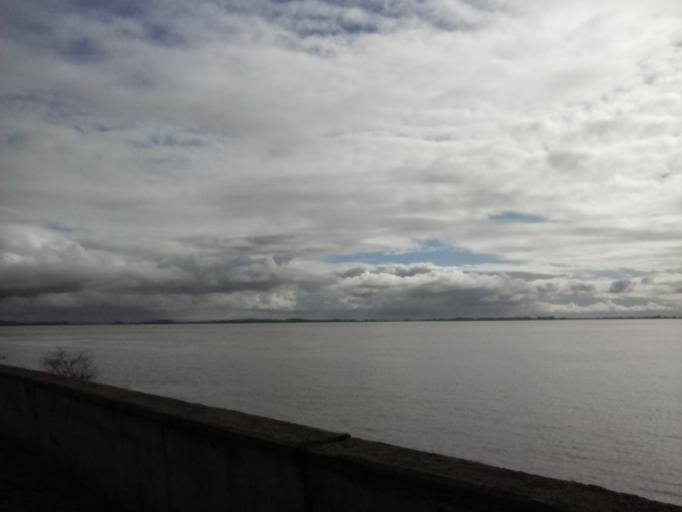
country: BR
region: Rio Grande do Sul
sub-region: Porto Alegre
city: Porto Alegre
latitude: -30.0775
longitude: -51.2455
